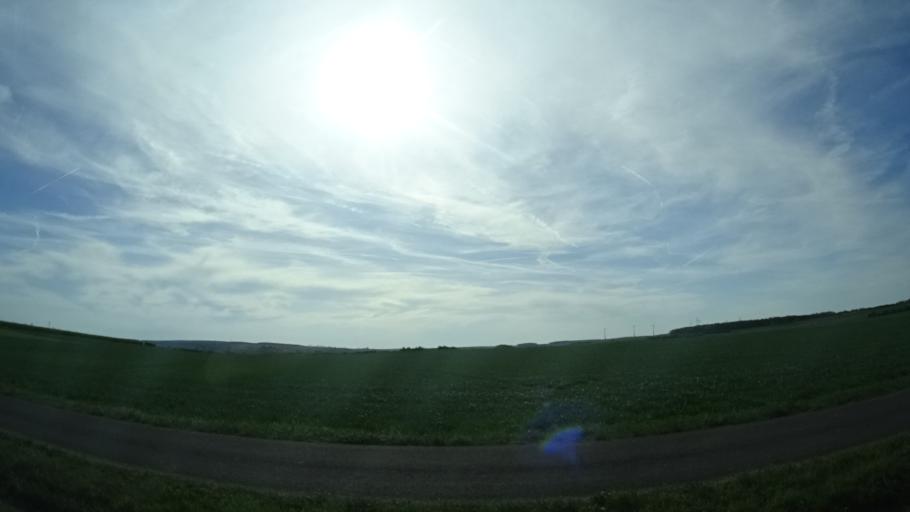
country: DE
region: Bavaria
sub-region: Regierungsbezirk Unterfranken
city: Volkach
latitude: 49.8813
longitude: 10.2283
